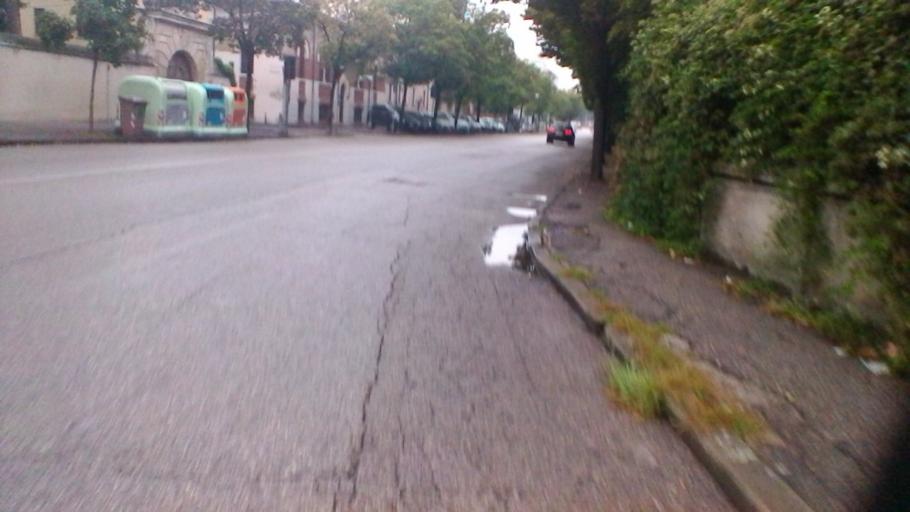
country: IT
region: Veneto
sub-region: Provincia di Verona
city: Verona
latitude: 45.4328
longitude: 10.9959
